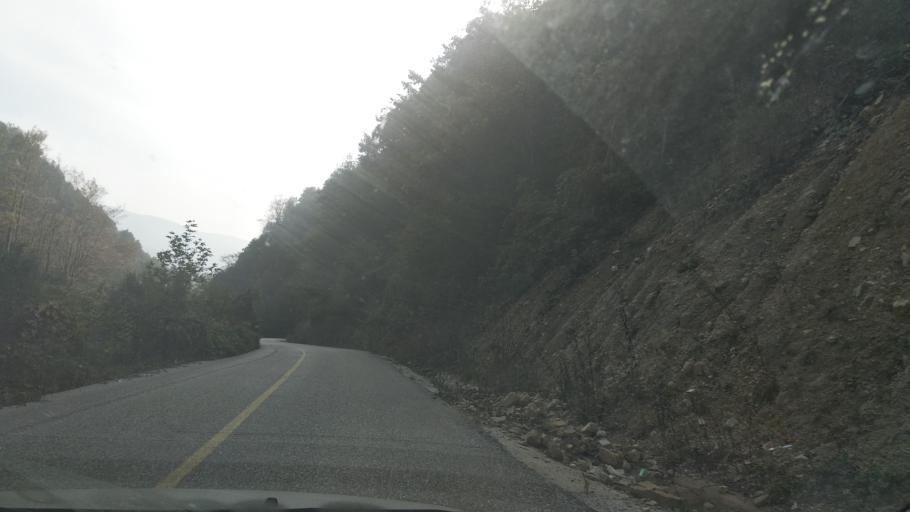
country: TR
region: Duzce
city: Kaynasli
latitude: 40.7247
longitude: 31.2616
